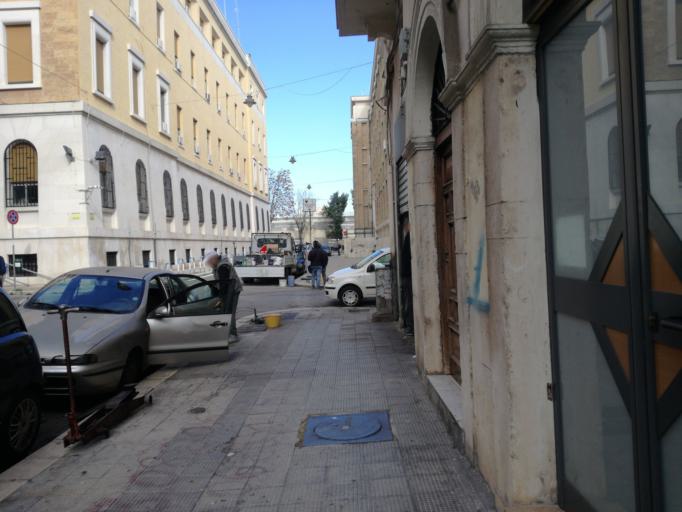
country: IT
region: Apulia
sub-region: Provincia di Bari
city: Bari
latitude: 41.1273
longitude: 16.8596
